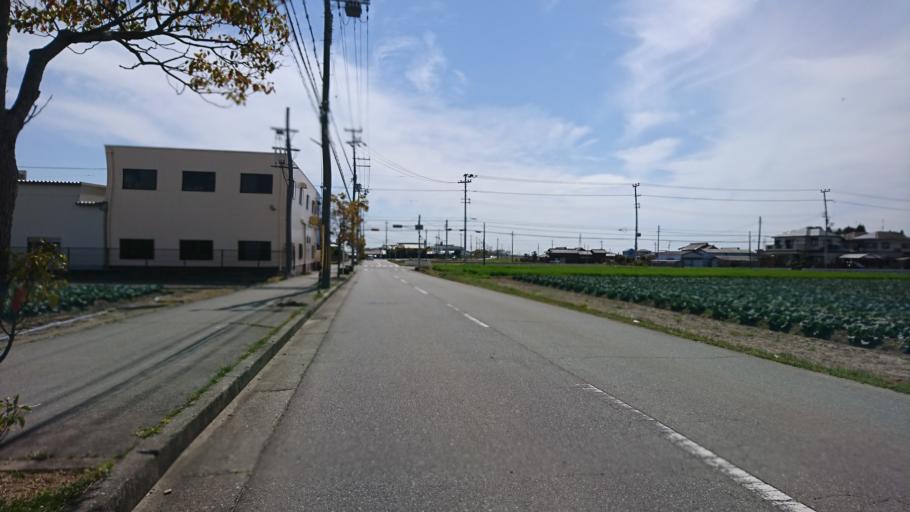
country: JP
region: Hyogo
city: Miki
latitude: 34.7491
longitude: 134.9315
